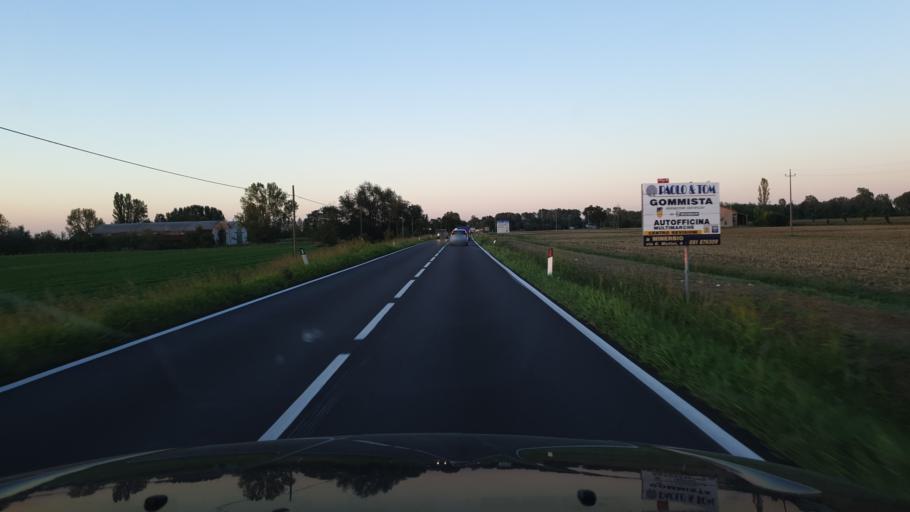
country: IT
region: Emilia-Romagna
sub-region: Provincia di Bologna
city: Ca De Fabbri
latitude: 44.5903
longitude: 11.4319
